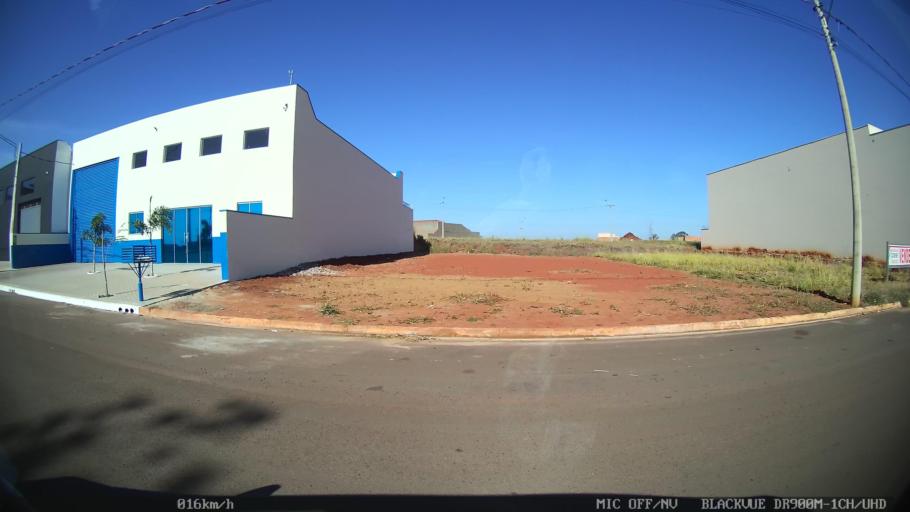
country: BR
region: Sao Paulo
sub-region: Olimpia
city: Olimpia
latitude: -20.7575
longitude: -48.9143
